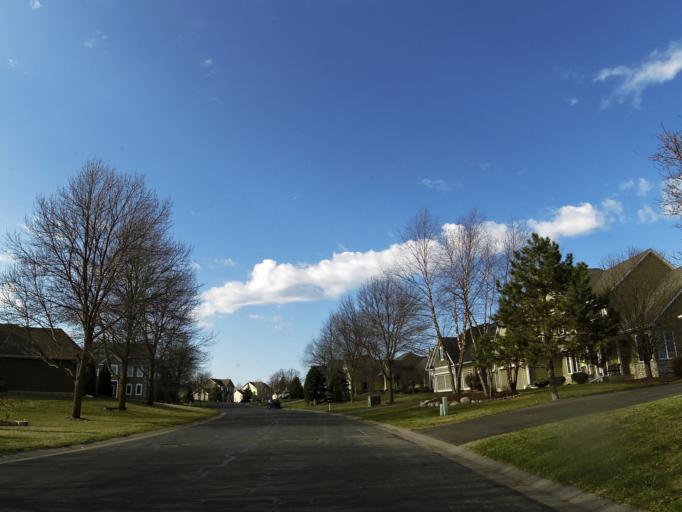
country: US
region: Minnesota
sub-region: Washington County
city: Woodbury
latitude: 44.8962
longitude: -92.8963
